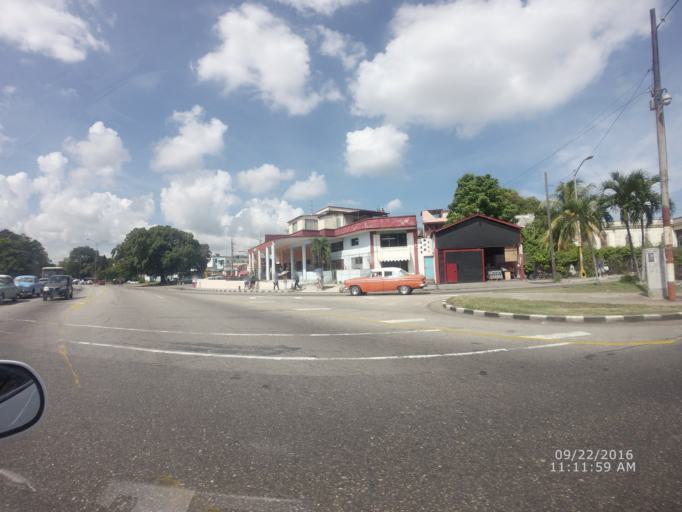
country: CU
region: La Habana
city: Cerro
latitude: 23.0939
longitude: -82.4217
